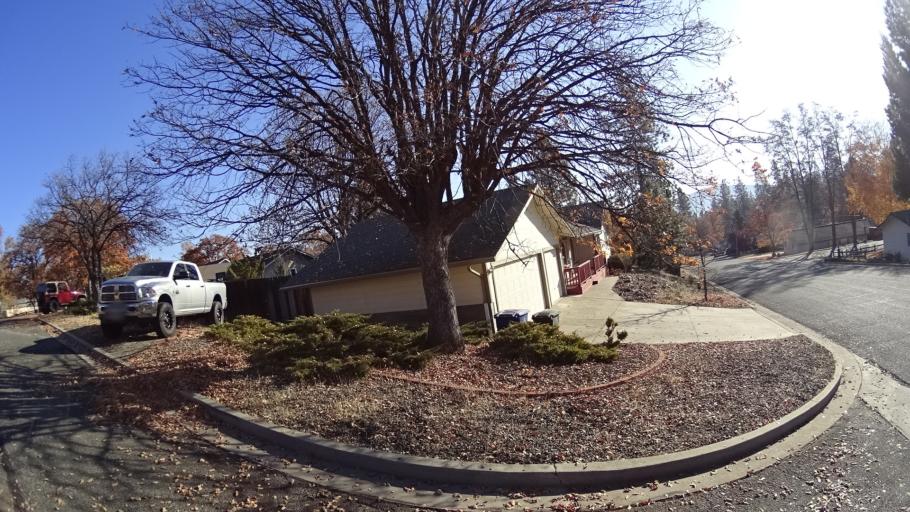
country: US
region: California
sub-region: Siskiyou County
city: Yreka
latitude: 41.7410
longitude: -122.6501
